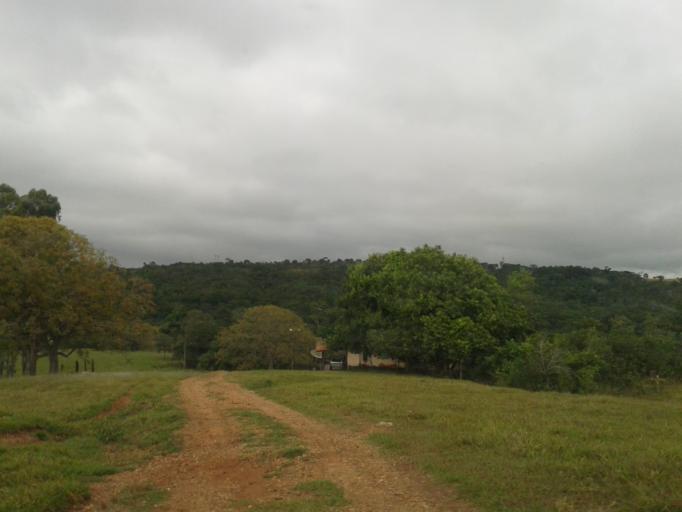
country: BR
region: Minas Gerais
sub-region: Campina Verde
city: Campina Verde
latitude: -19.4230
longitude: -49.6303
